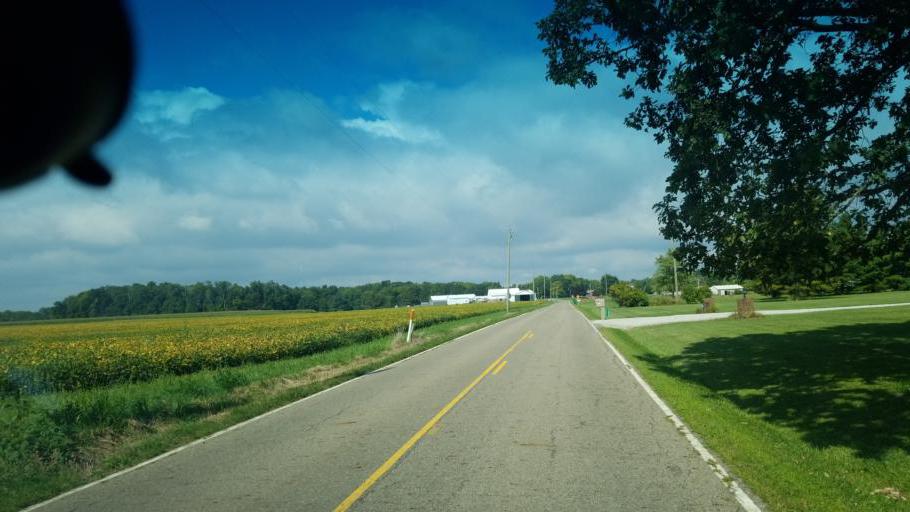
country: US
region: Ohio
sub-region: Licking County
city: Johnstown
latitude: 40.2286
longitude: -82.6382
